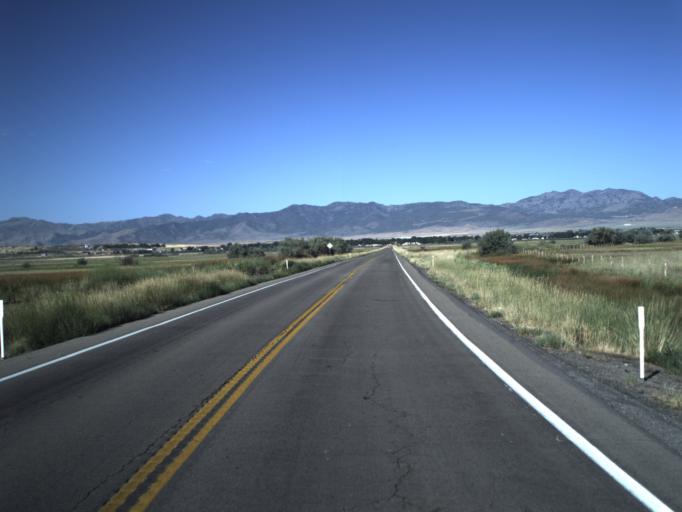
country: US
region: Utah
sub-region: Utah County
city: Genola
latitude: 39.9604
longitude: -111.8668
